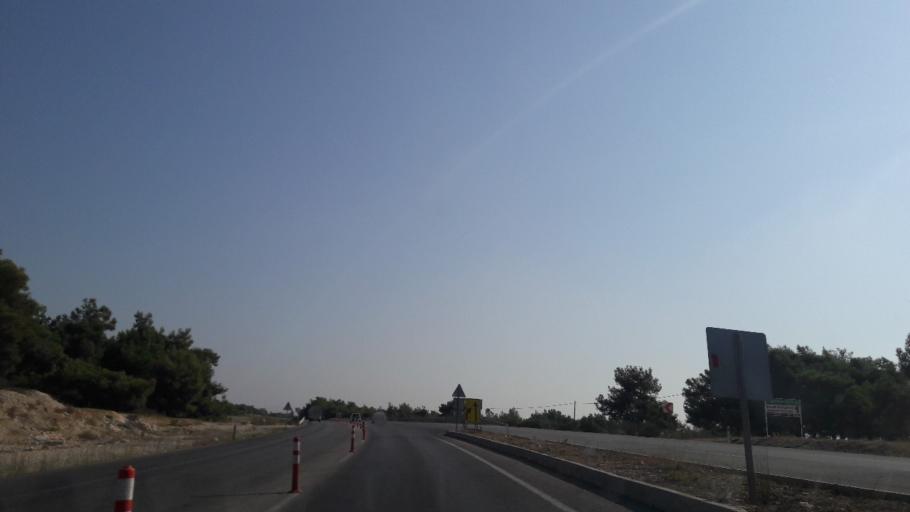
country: TR
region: Adana
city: Yuregir
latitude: 37.0823
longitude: 35.4792
